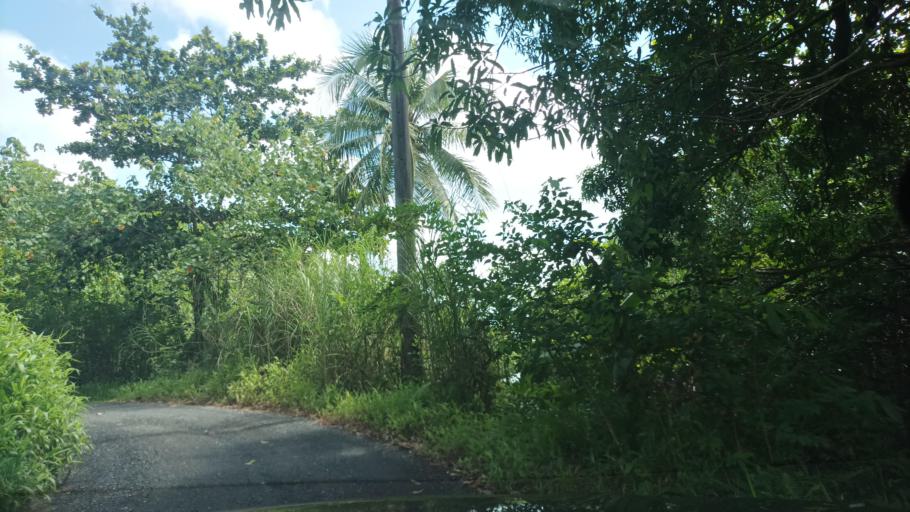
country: FM
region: Pohnpei
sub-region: Sokehs Municipality
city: Palikir - National Government Center
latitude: 6.9428
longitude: 158.1635
